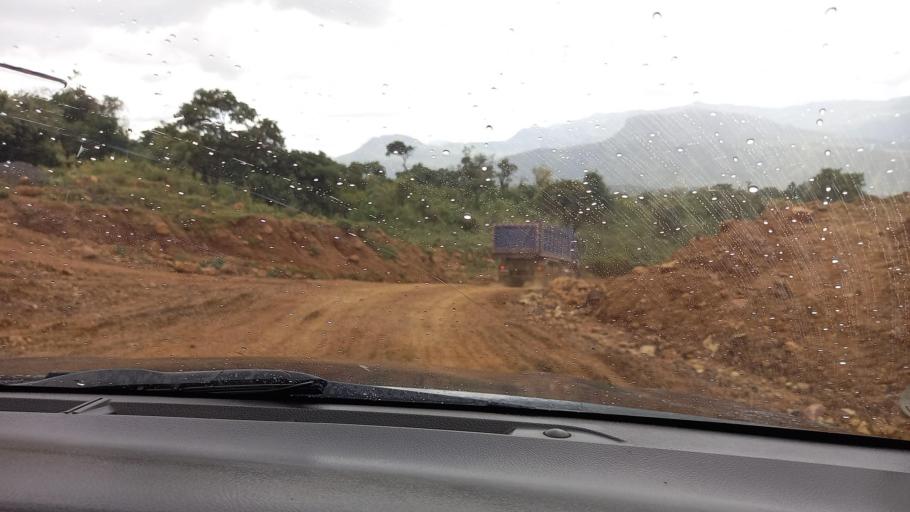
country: ET
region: Southern Nations, Nationalities, and People's Region
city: Mizan Teferi
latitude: 6.1750
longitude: 35.7133
